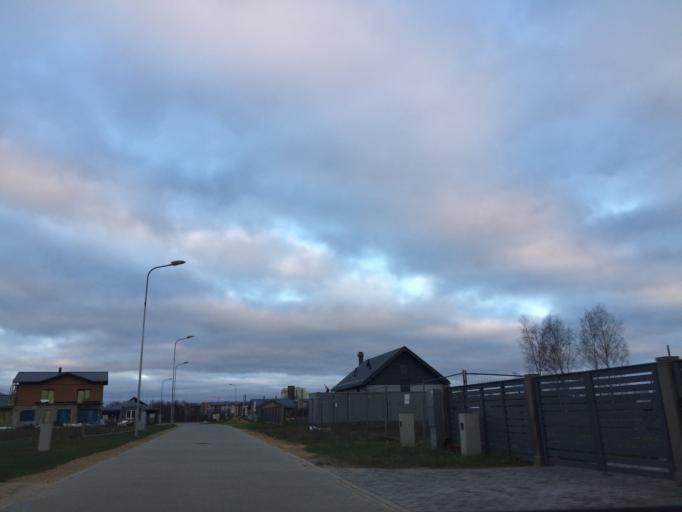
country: LV
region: Adazi
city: Adazi
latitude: 57.0664
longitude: 24.3457
